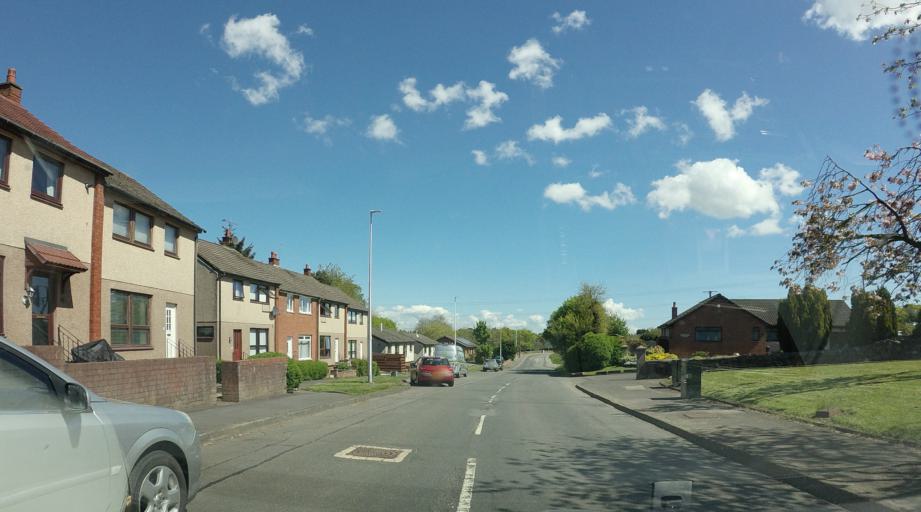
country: GB
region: Scotland
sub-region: Falkirk
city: Polmont
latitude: 55.9715
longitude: -3.6952
